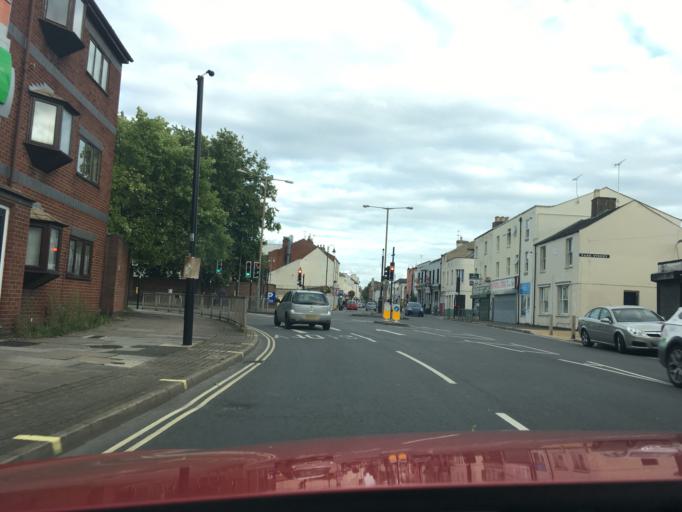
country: GB
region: England
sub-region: Gloucestershire
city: Cheltenham
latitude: 51.9049
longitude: -2.0835
